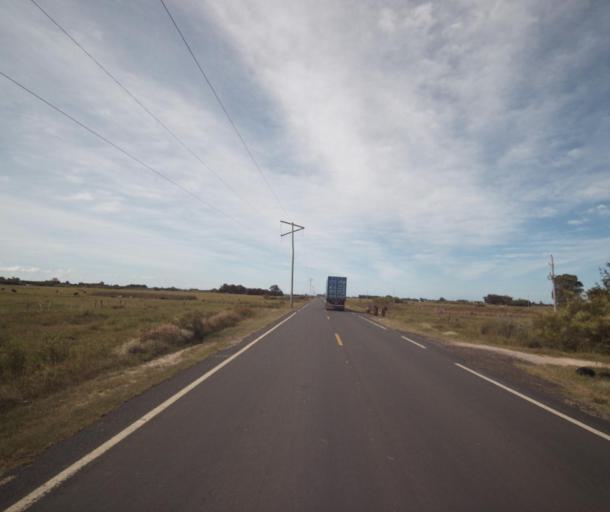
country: BR
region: Rio Grande do Sul
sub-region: Rio Grande
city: Rio Grande
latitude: -31.9408
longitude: -51.9722
